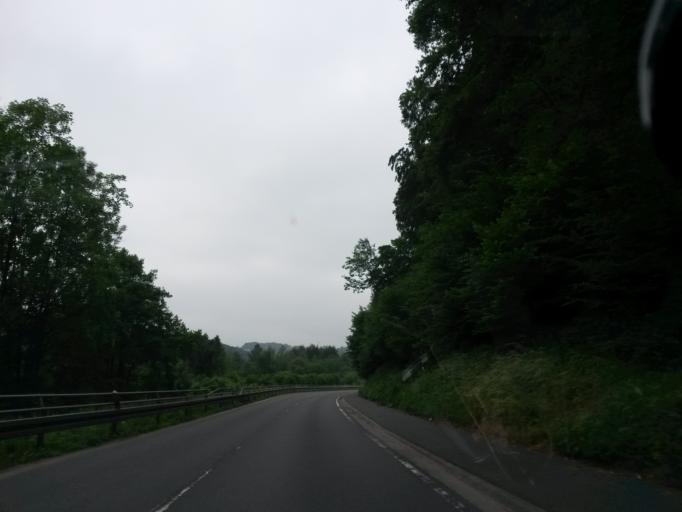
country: DE
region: North Rhine-Westphalia
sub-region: Regierungsbezirk Koln
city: Overath
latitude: 50.9530
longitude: 7.3099
